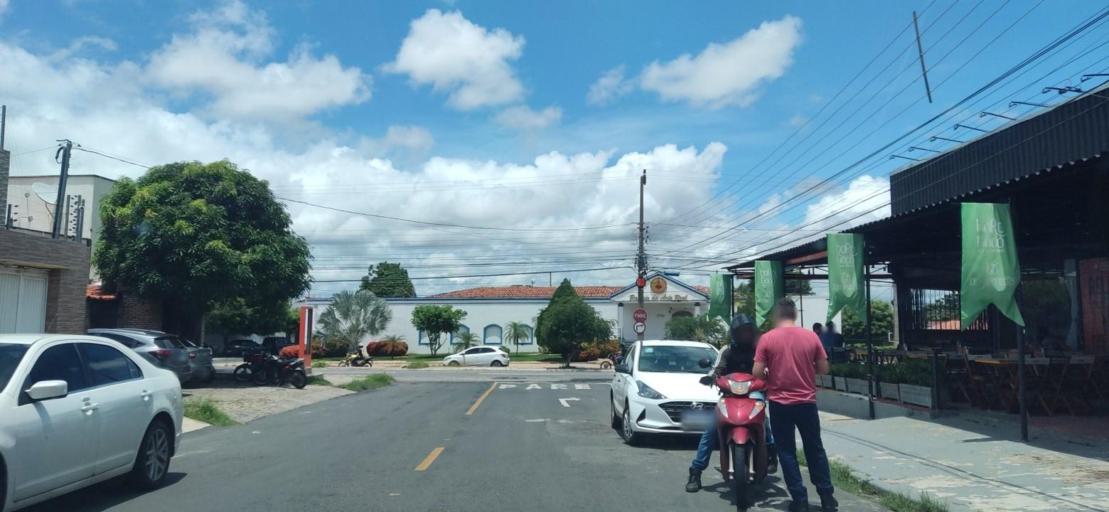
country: BR
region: Piaui
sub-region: Teresina
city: Teresina
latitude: -5.0703
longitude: -42.7665
